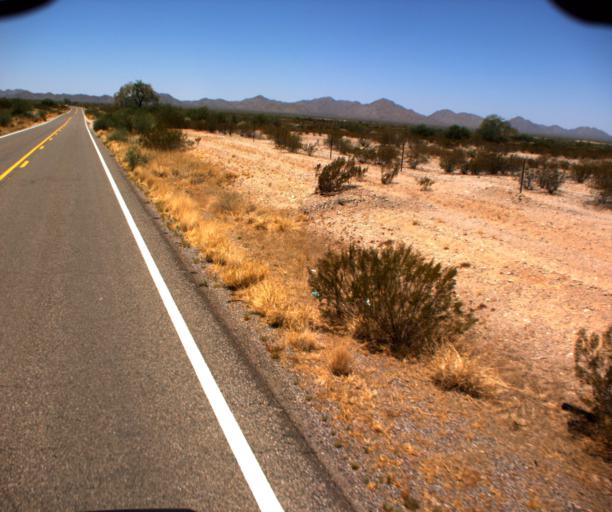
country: US
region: Arizona
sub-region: Pinal County
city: Maricopa
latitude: 33.0327
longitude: -112.3585
